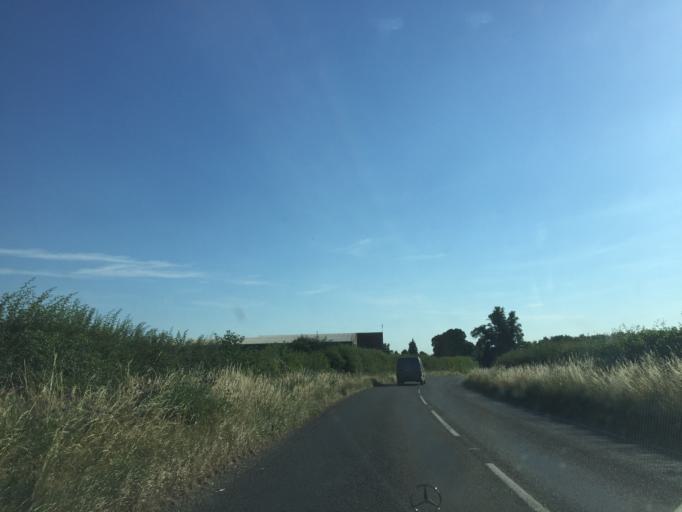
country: GB
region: England
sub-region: Oxfordshire
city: Watlington
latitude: 51.6676
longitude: -0.9758
